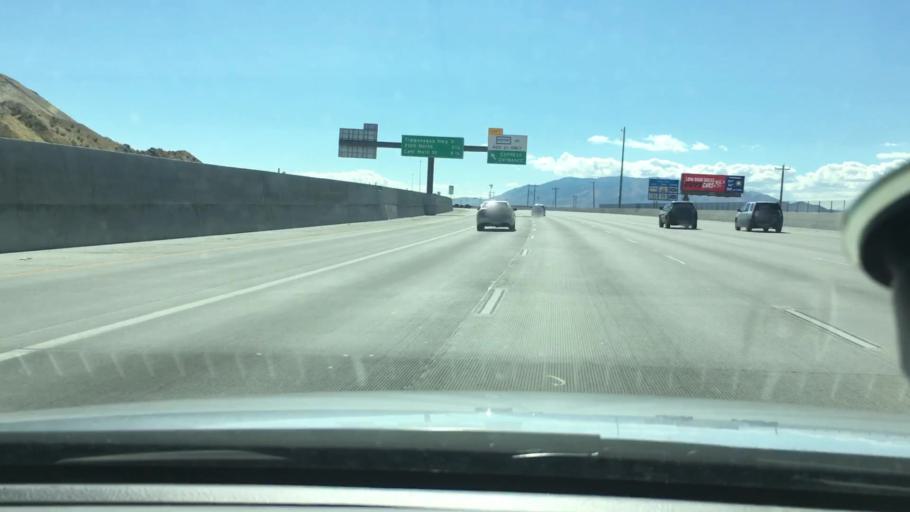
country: US
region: Utah
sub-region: Salt Lake County
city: Bluffdale
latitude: 40.4594
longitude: -111.9146
